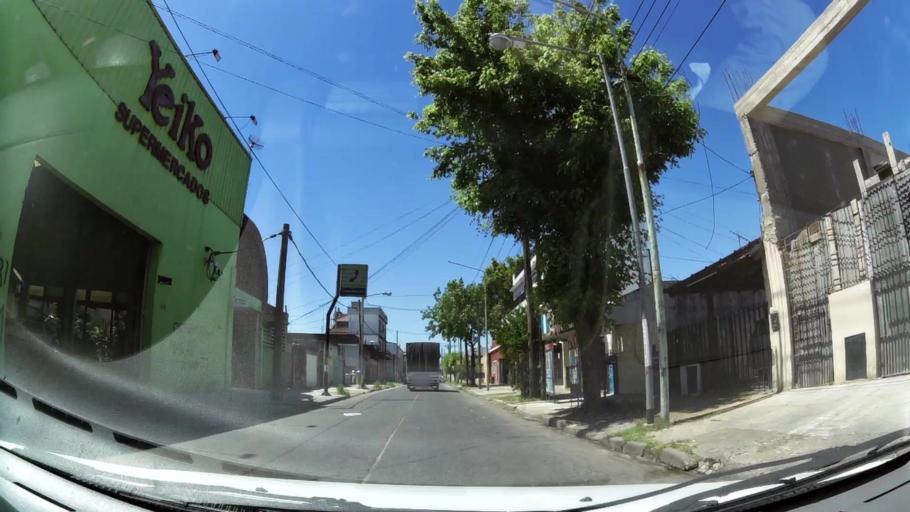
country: AR
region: Buenos Aires
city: Caseros
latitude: -34.5830
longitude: -58.5674
